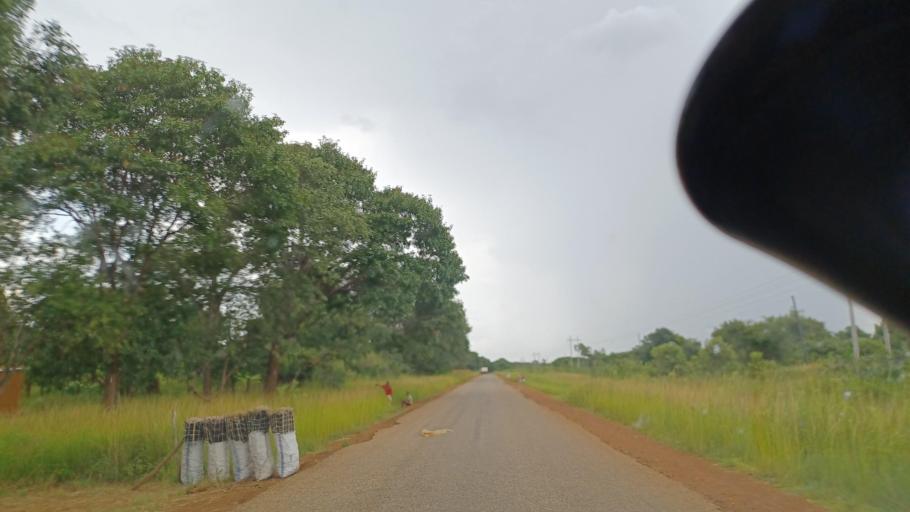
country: ZM
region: North-Western
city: Kasempa
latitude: -13.0416
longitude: 25.9930
